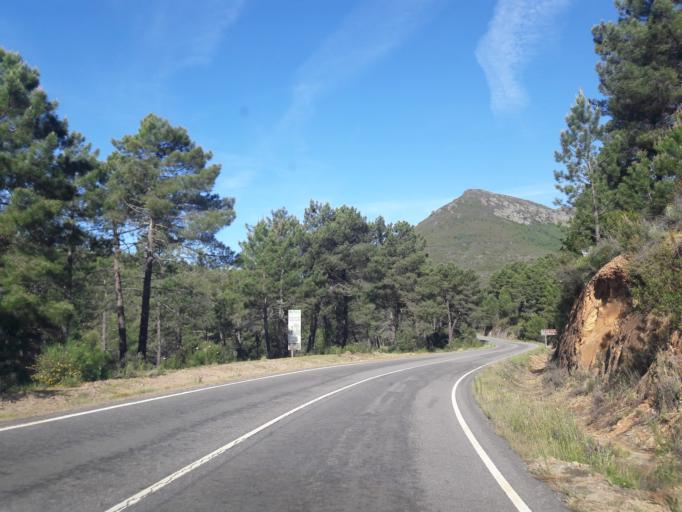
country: ES
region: Castille and Leon
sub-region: Provincia de Salamanca
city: Sotoserrano
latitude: 40.4114
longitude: -6.0423
